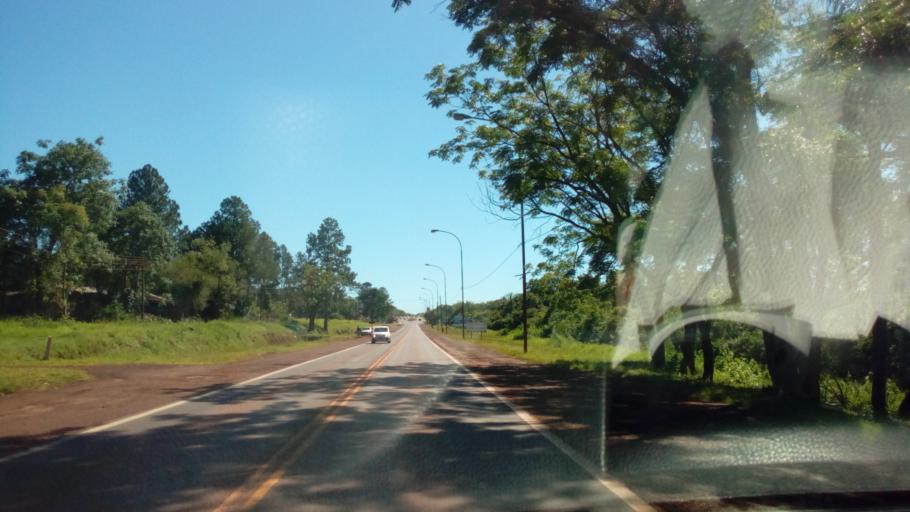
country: AR
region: Misiones
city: Santa Ana
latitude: -27.3804
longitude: -55.5826
